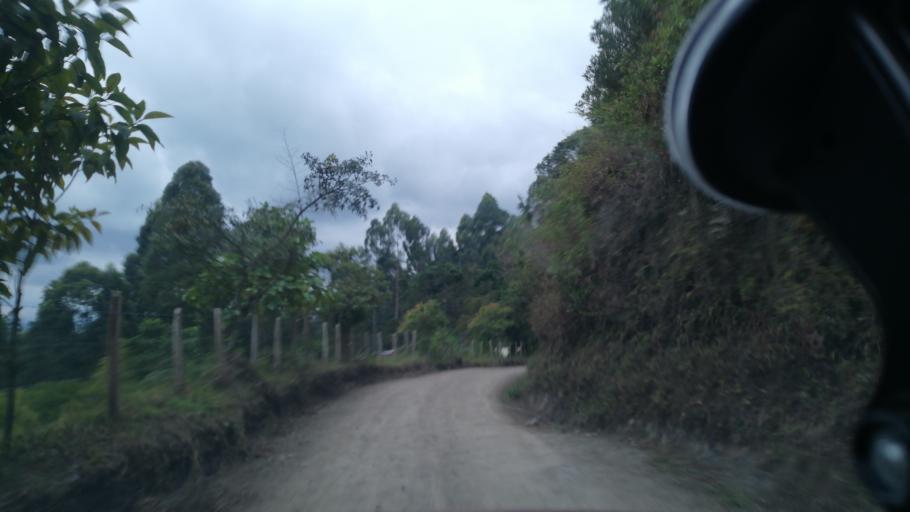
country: CO
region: Cundinamarca
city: Pacho
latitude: 5.1577
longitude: -74.2541
